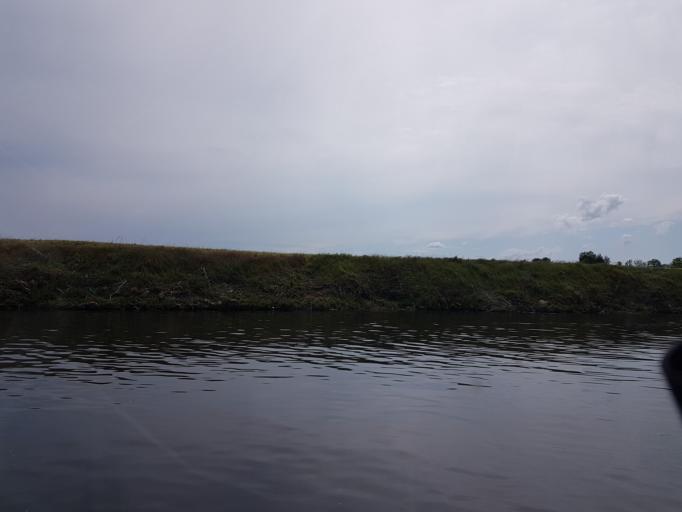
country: FR
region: Bourgogne
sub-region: Departement de l'Yonne
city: Moneteau
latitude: 47.8516
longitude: 3.5672
